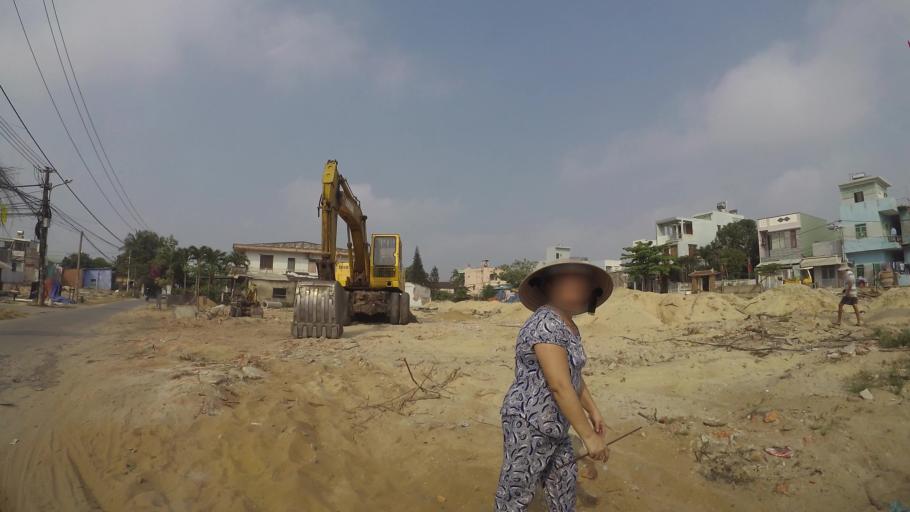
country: VN
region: Da Nang
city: Ngu Hanh Son
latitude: 16.0247
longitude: 108.2465
